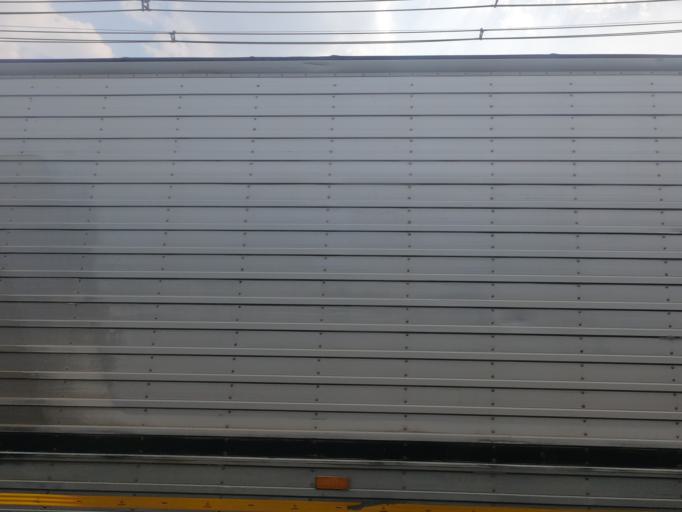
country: TH
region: Nakhon Ratchasima
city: Amphoe Sikhiu
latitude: 14.8581
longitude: 101.6809
